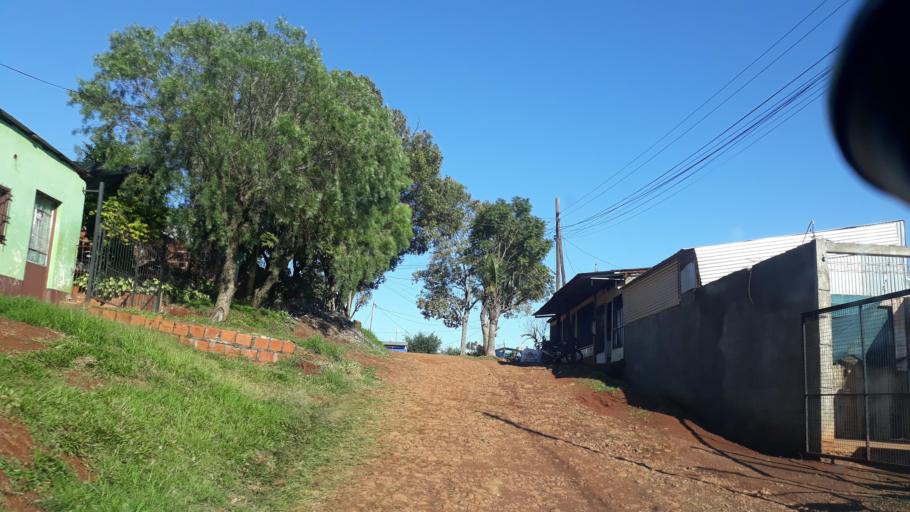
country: AR
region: Misiones
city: Bernardo de Irigoyen
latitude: -26.2613
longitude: -53.6527
